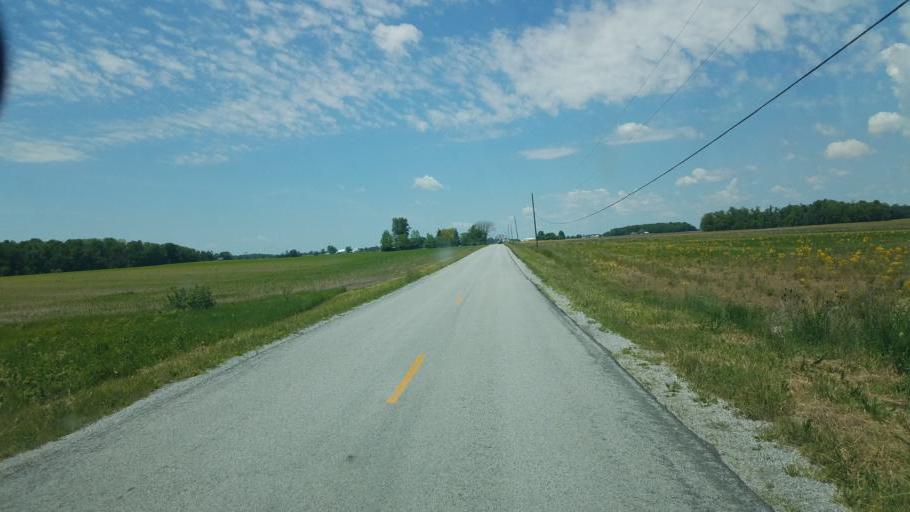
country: US
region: Ohio
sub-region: Hardin County
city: Forest
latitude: 40.6807
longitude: -83.4248
